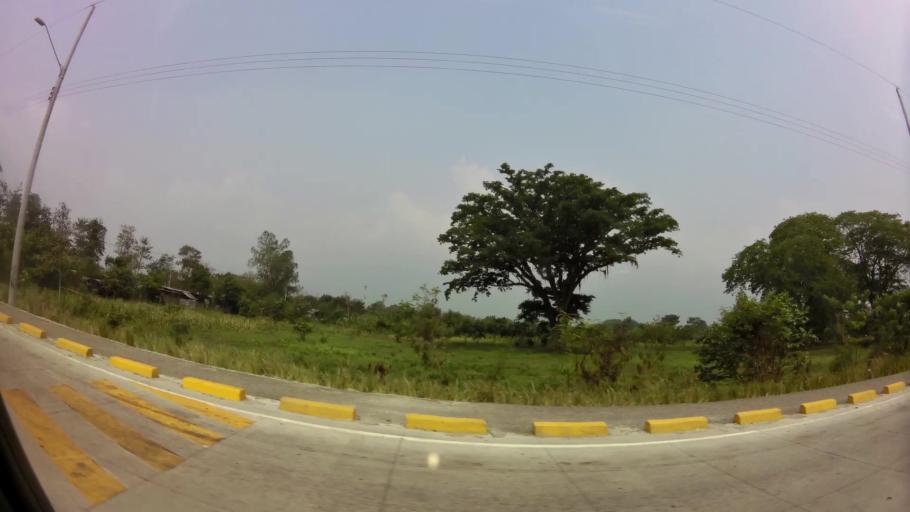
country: HN
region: Cortes
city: San Pedro Sula
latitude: 15.5172
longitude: -88.0023
